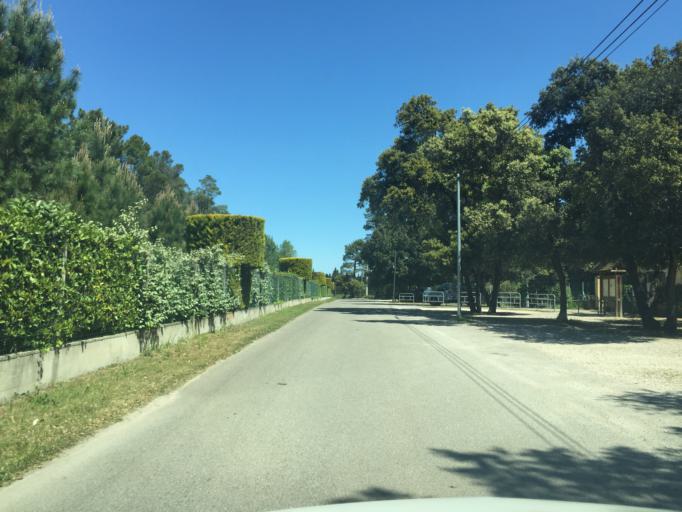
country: FR
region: Provence-Alpes-Cote d'Azur
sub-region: Departement du Vaucluse
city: Orange
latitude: 44.1052
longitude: 4.7984
